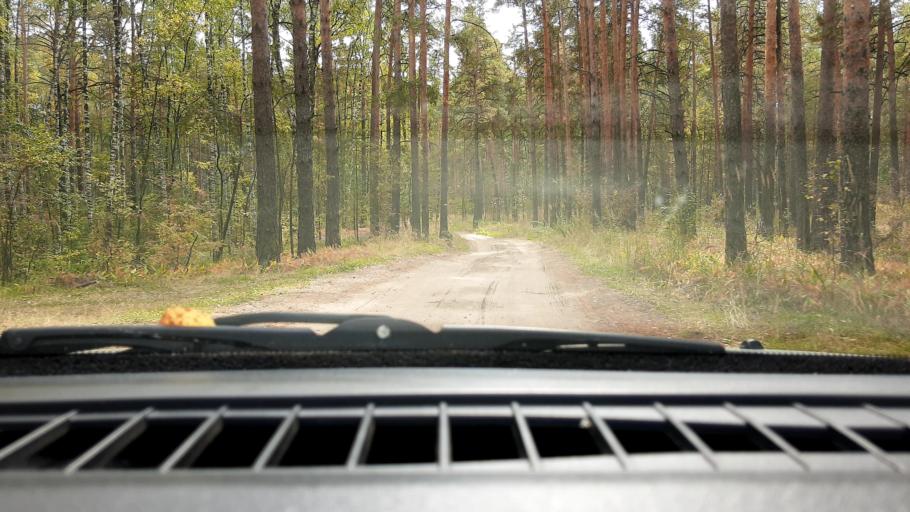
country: RU
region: Nizjnij Novgorod
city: Gorbatovka
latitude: 56.3231
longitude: 43.6918
